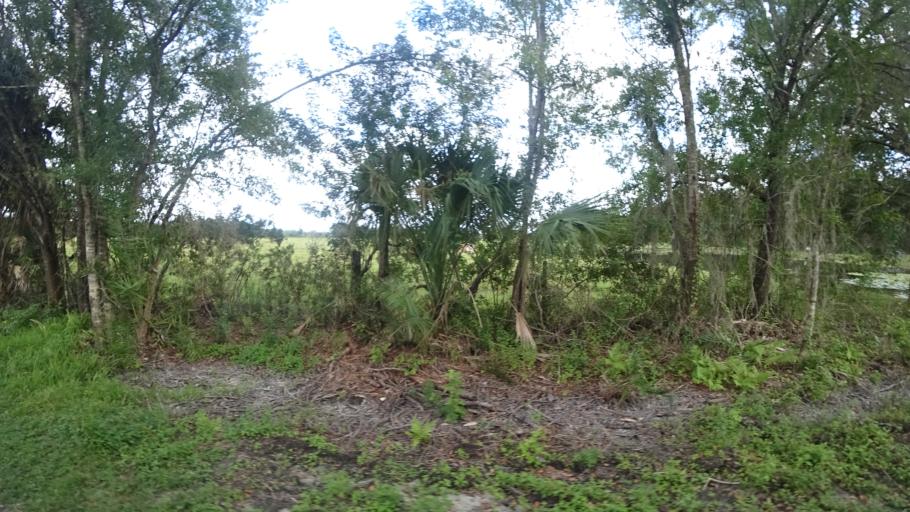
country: US
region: Florida
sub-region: Sarasota County
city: Lake Sarasota
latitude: 27.3944
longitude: -82.2664
